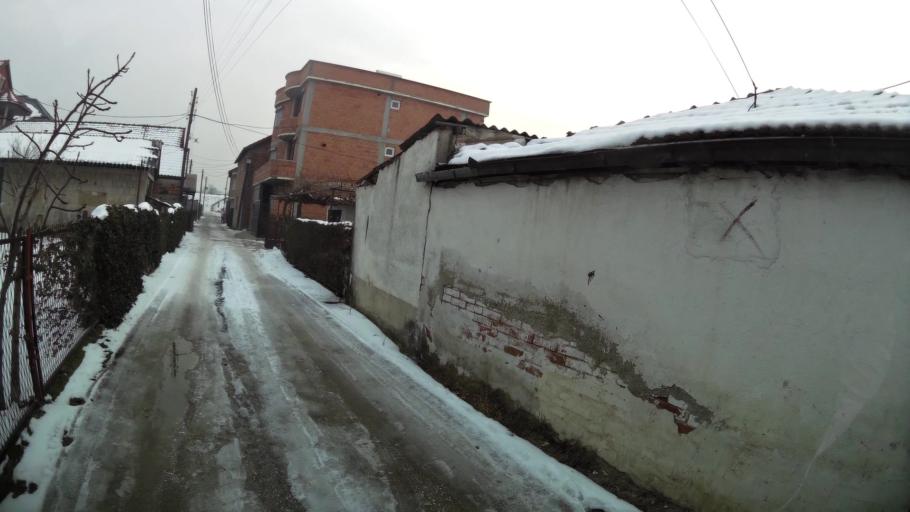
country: MK
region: Suto Orizari
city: Suto Orizare
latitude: 42.0286
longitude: 21.4307
